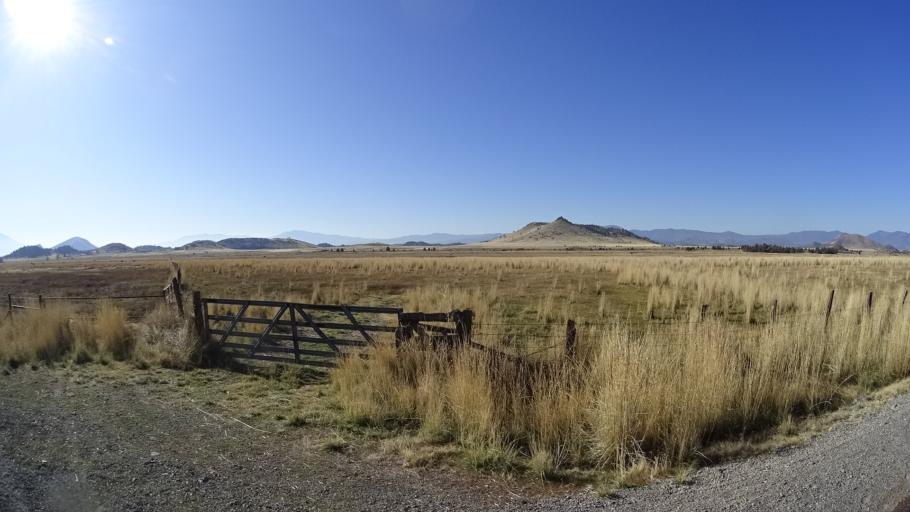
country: US
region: California
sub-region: Siskiyou County
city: Montague
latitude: 41.7152
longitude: -122.4428
